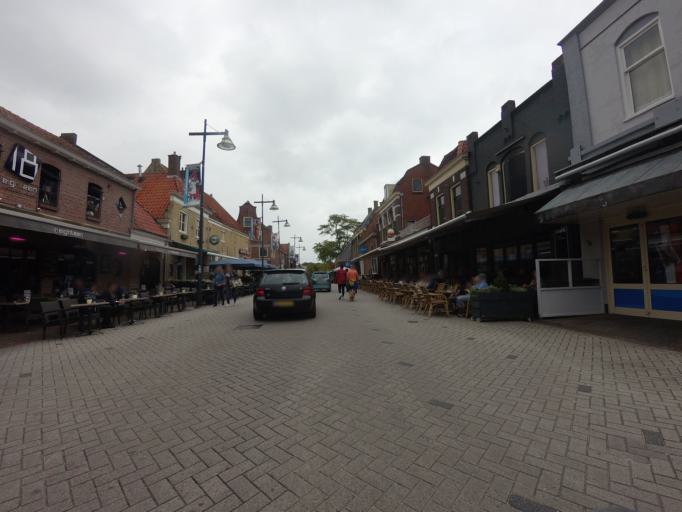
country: NL
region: North Holland
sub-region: Gemeente Enkhuizen
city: Enkhuizen
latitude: 52.7034
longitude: 5.2901
